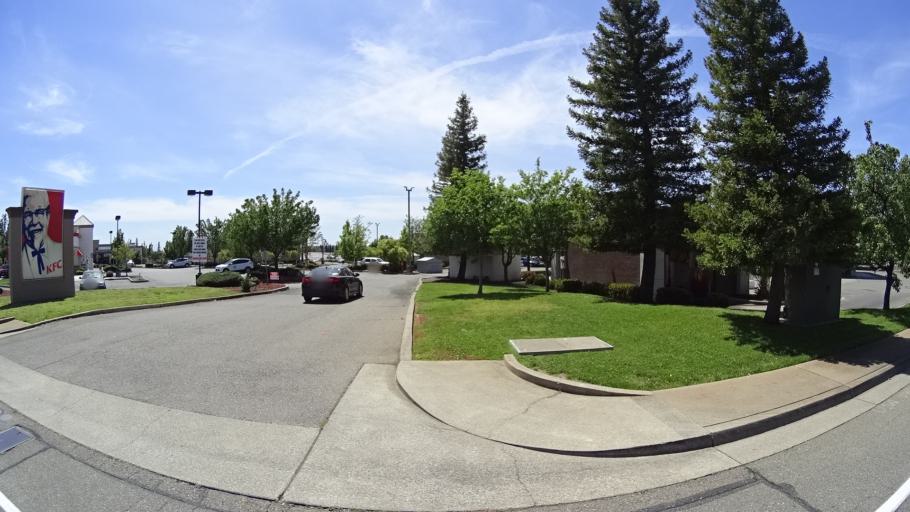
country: US
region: California
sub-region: Placer County
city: Rocklin
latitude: 38.7811
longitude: -121.2643
